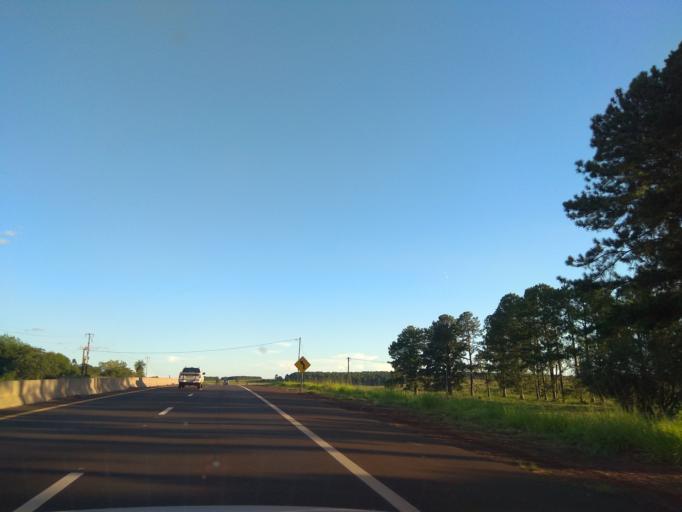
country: AR
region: Misiones
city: Garupa
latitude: -27.5561
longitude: -55.8499
